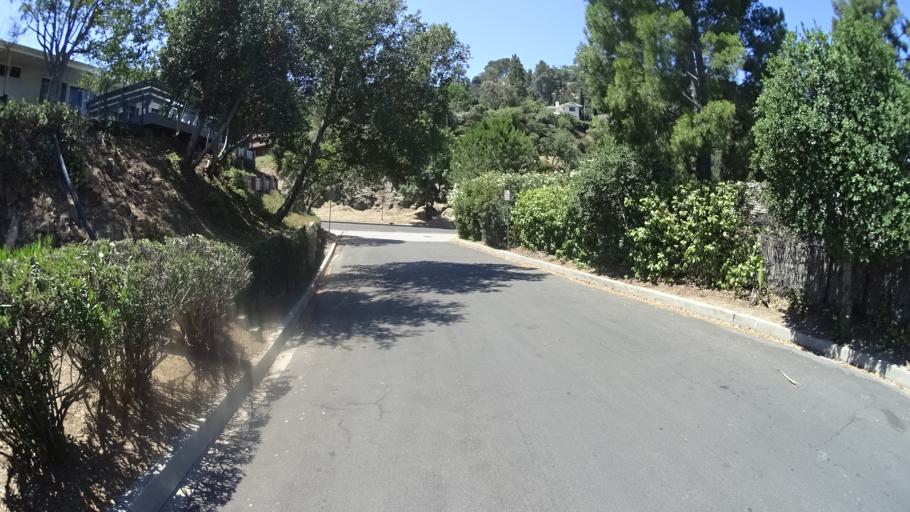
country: US
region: California
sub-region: Los Angeles County
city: Universal City
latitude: 34.1336
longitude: -118.3696
